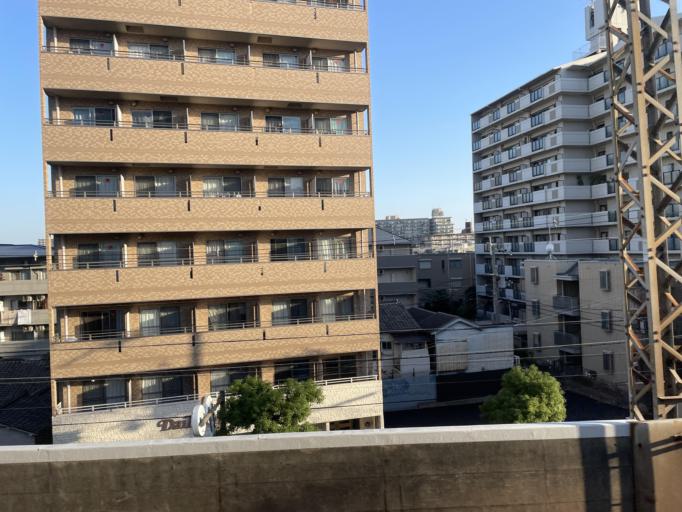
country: JP
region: Osaka
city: Yao
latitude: 34.6642
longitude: 135.5771
